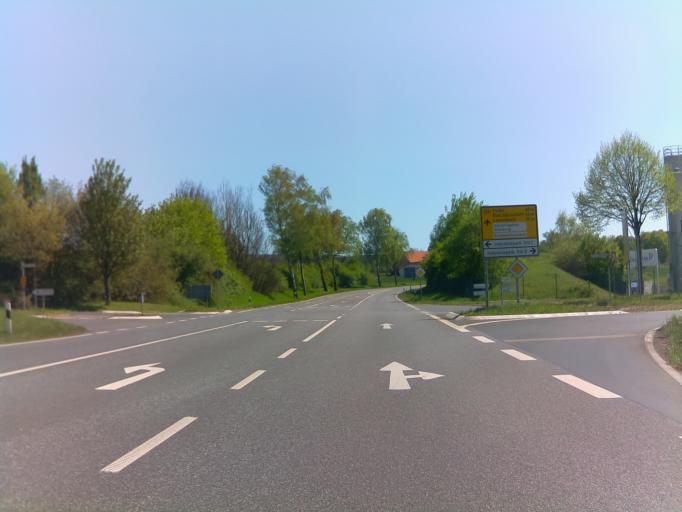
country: DE
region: Hesse
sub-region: Regierungsbezirk Giessen
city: Alsfeld
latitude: 50.7479
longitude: 9.2873
